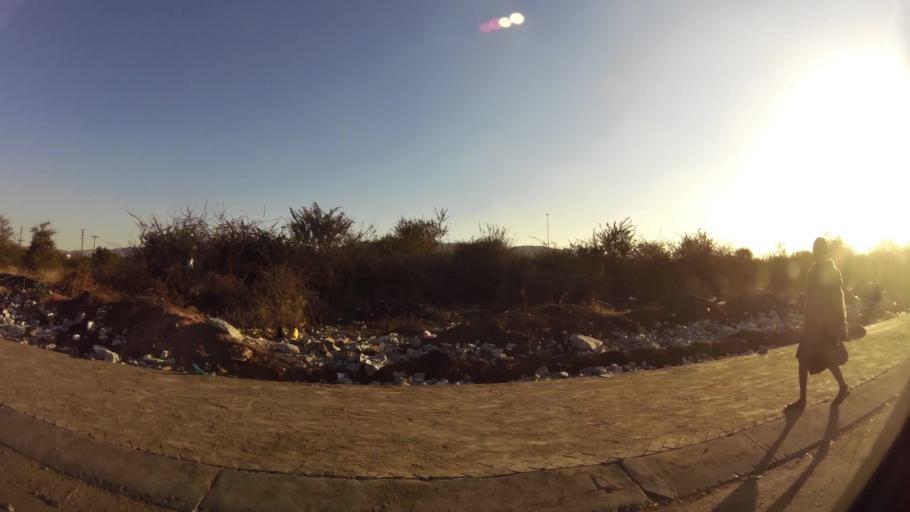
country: ZA
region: North-West
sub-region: Bojanala Platinum District Municipality
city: Rustenburg
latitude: -25.6332
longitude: 27.2213
